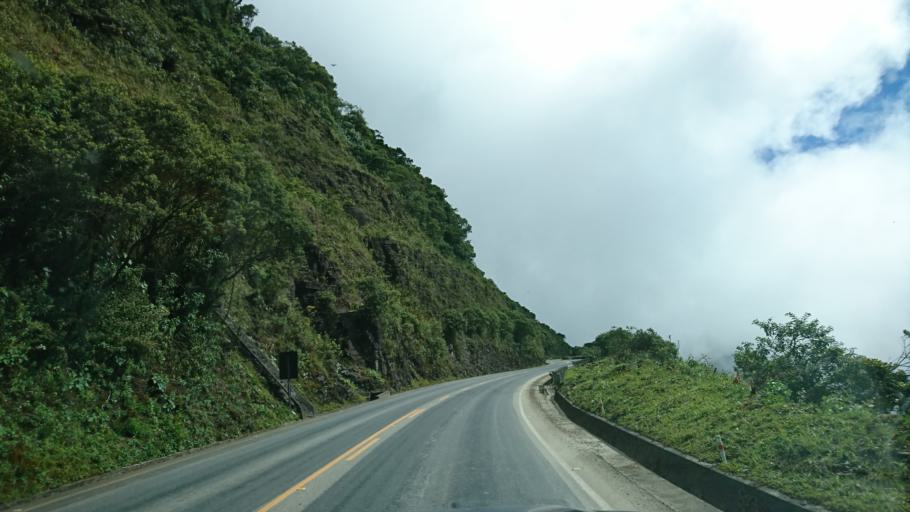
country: BO
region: La Paz
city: Coroico
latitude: -16.2268
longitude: -67.8324
